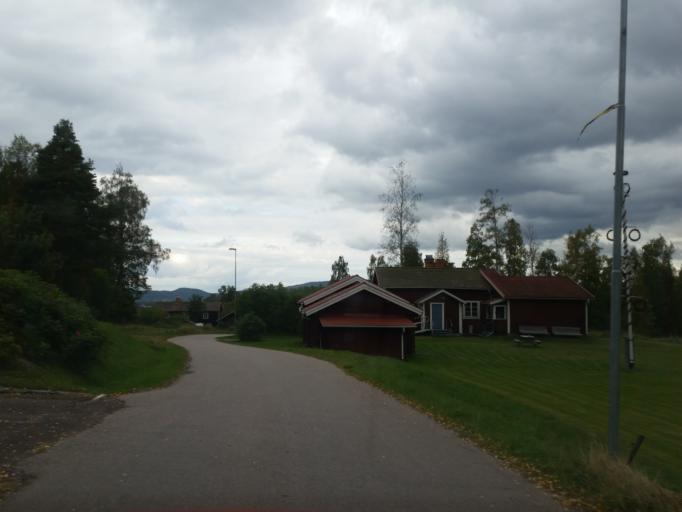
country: SE
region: Dalarna
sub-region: Leksand Municipality
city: Smedby
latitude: 60.6721
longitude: 15.1266
